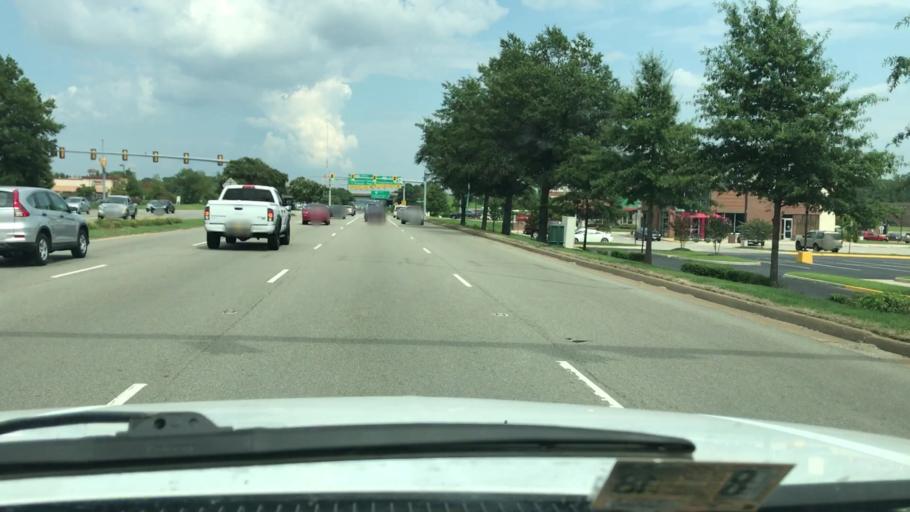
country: US
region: Virginia
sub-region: Chesterfield County
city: Bon Air
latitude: 37.5006
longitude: -77.5292
